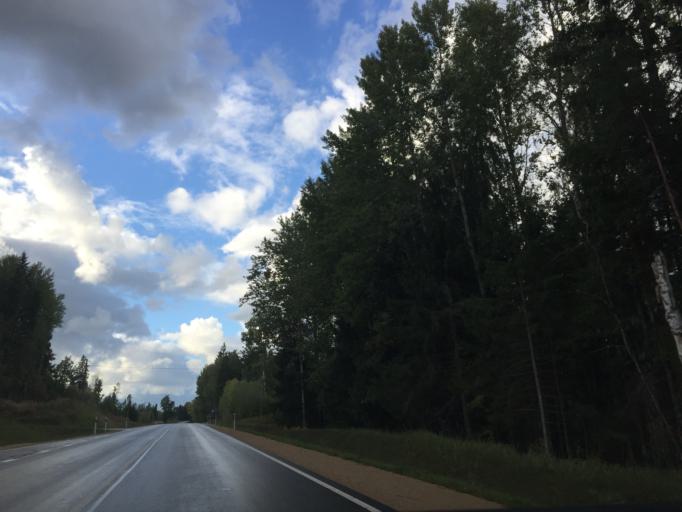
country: LV
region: Ligatne
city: Ligatne
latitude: 57.1598
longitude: 25.0590
